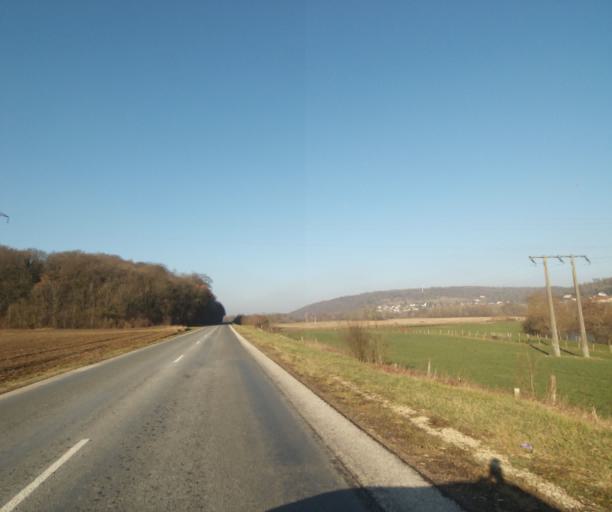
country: FR
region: Champagne-Ardenne
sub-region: Departement de la Haute-Marne
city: Chevillon
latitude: 48.5136
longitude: 5.1109
